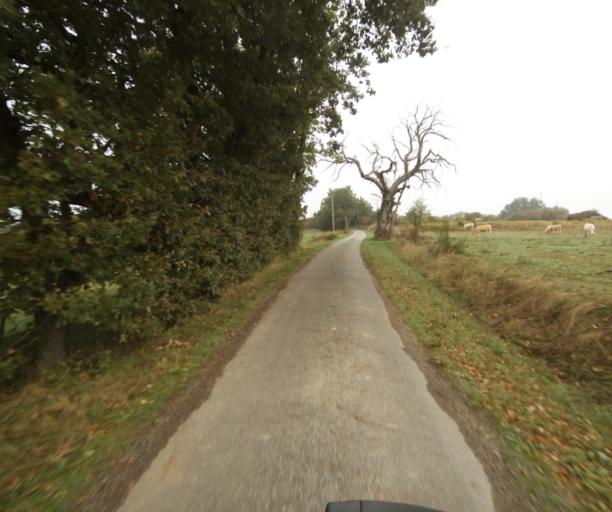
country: FR
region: Midi-Pyrenees
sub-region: Departement du Tarn-et-Garonne
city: Nohic
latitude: 43.9272
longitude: 1.4700
